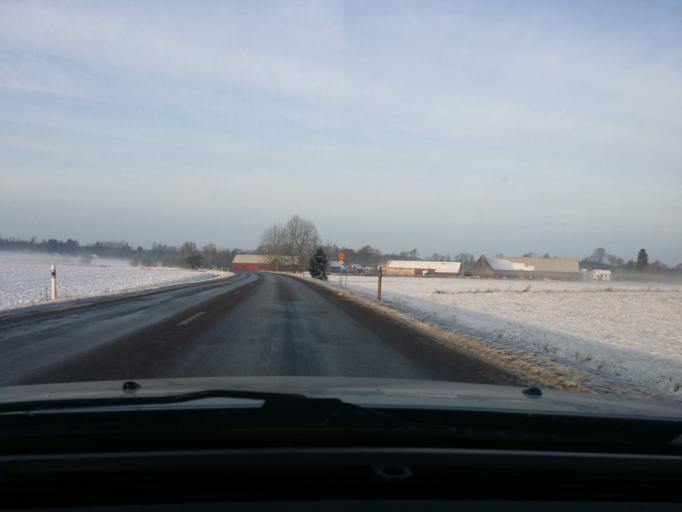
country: SE
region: OErebro
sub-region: Lindesbergs Kommun
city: Fellingsbro
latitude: 59.4689
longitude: 15.5441
